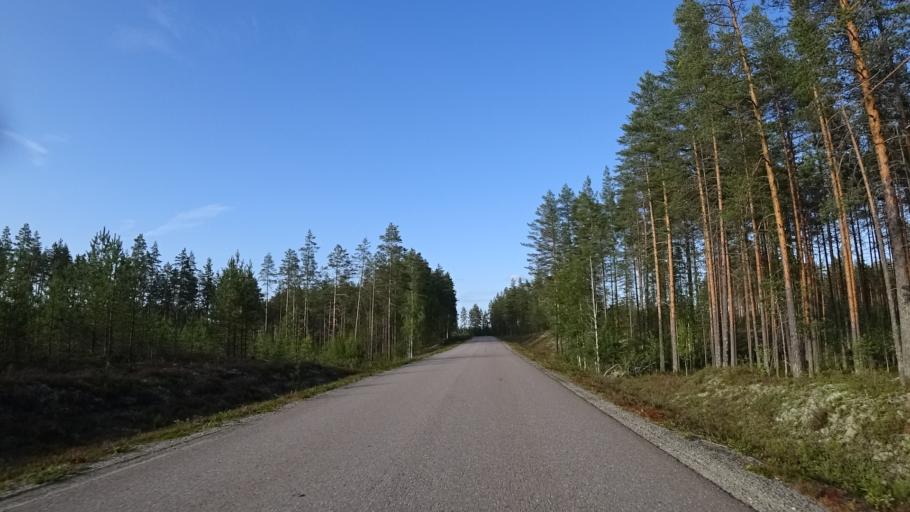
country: FI
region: North Karelia
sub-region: Joensuu
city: Eno
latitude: 63.0814
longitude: 30.5860
